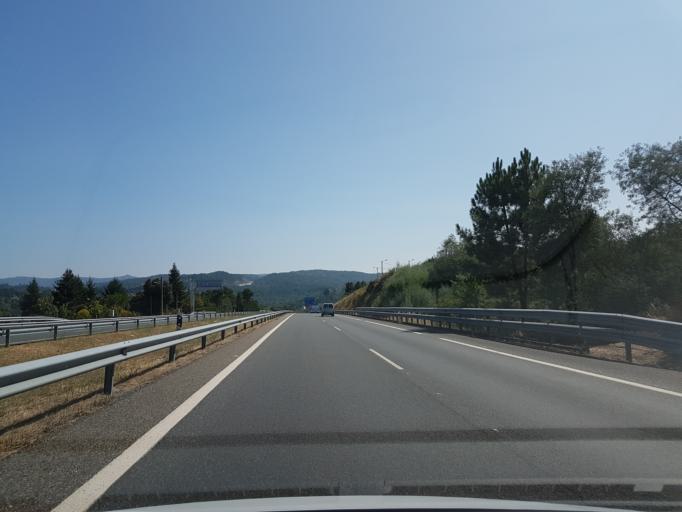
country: ES
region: Galicia
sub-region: Provincia de Ourense
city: Ourense
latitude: 42.3216
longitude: -7.8871
